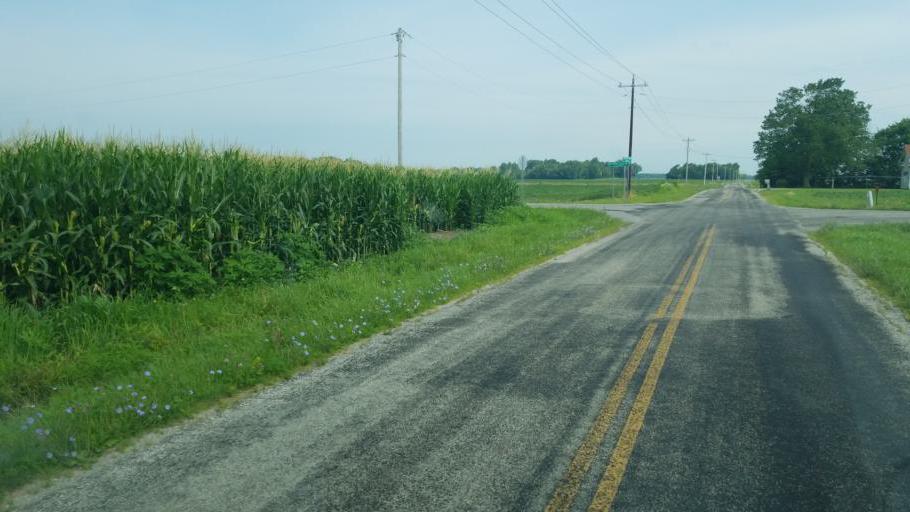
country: US
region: Ohio
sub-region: Wyandot County
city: Upper Sandusky
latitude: 40.6728
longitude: -83.2956
